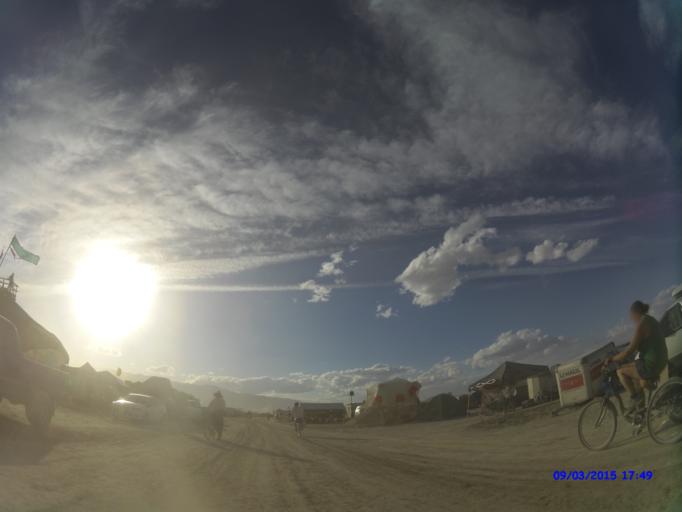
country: US
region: Nevada
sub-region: Pershing County
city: Lovelock
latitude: 40.7750
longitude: -119.2116
